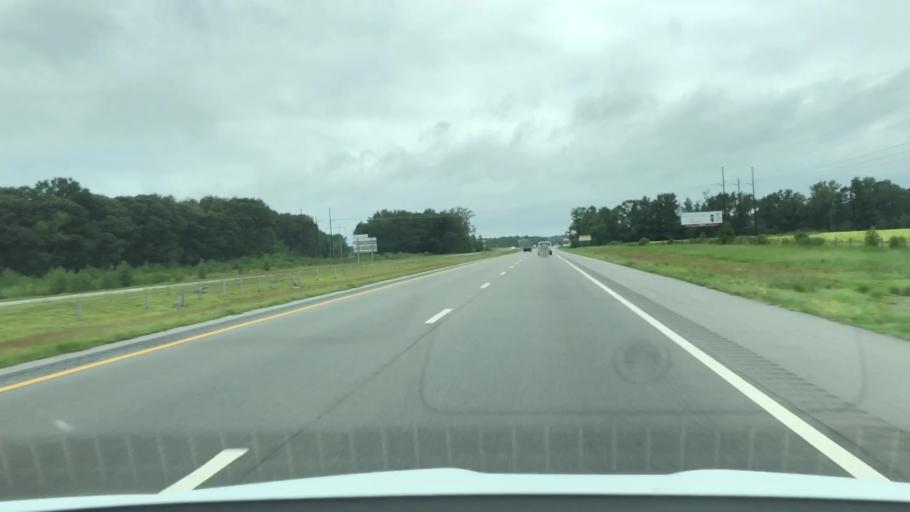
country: US
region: North Carolina
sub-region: Lenoir County
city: La Grange
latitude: 35.3183
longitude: -77.8323
